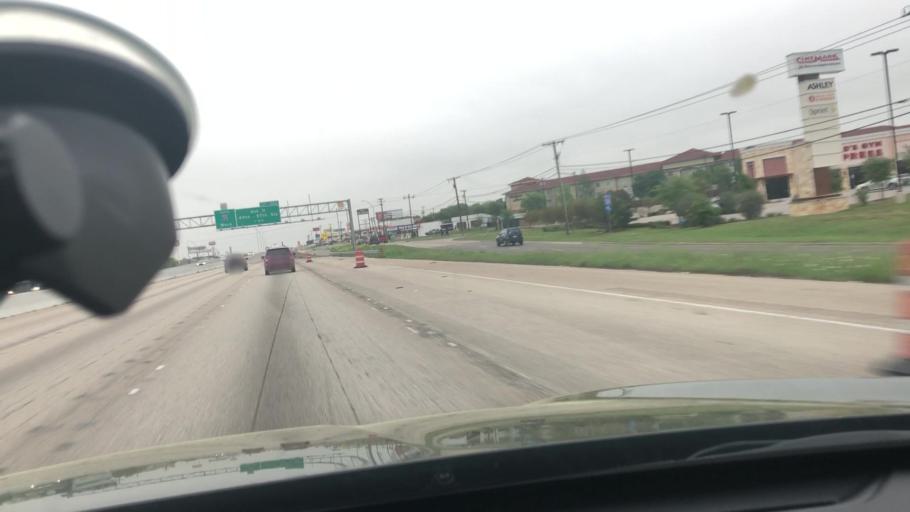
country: US
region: Texas
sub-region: Bell County
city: Temple
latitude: 31.0872
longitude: -97.3980
